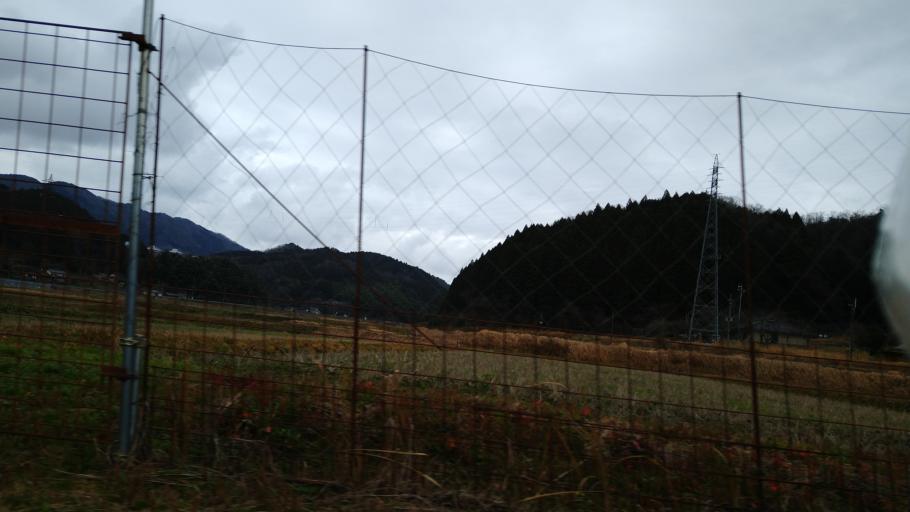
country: JP
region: Kyoto
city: Ayabe
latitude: 35.3334
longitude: 135.3494
